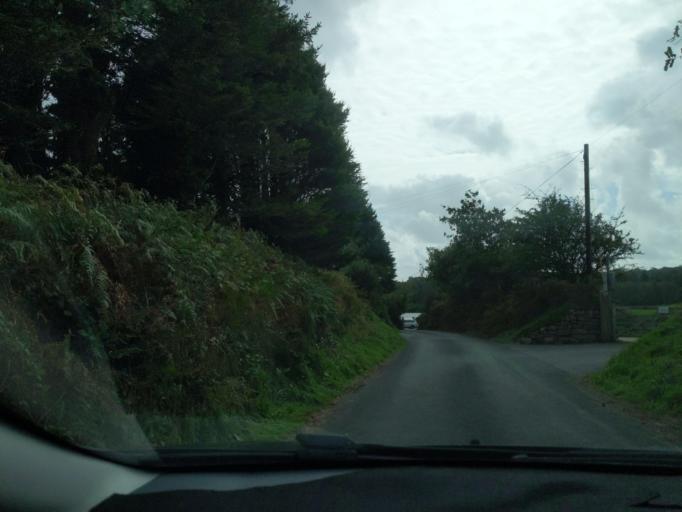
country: GB
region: England
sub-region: Cornwall
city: Lostwithiel
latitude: 50.3984
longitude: -4.7035
